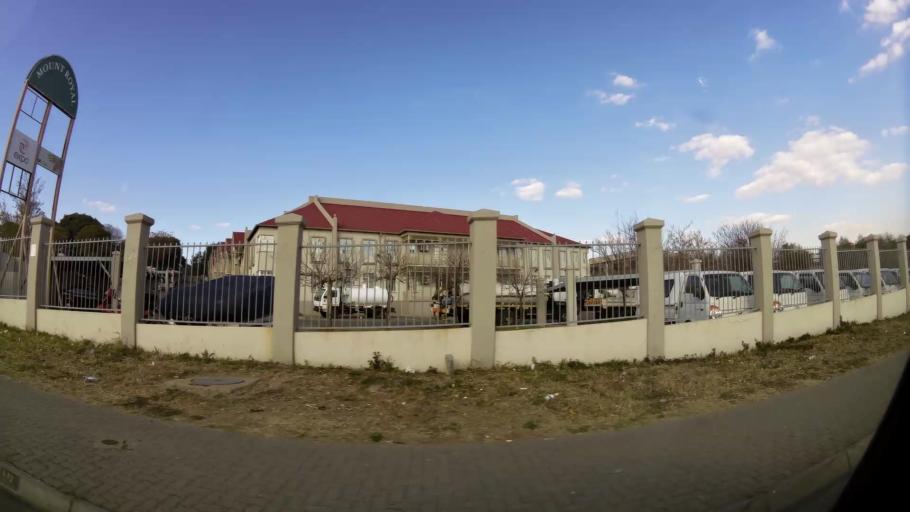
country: ZA
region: Gauteng
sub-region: City of Johannesburg Metropolitan Municipality
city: Midrand
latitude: -26.0049
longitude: 28.1234
